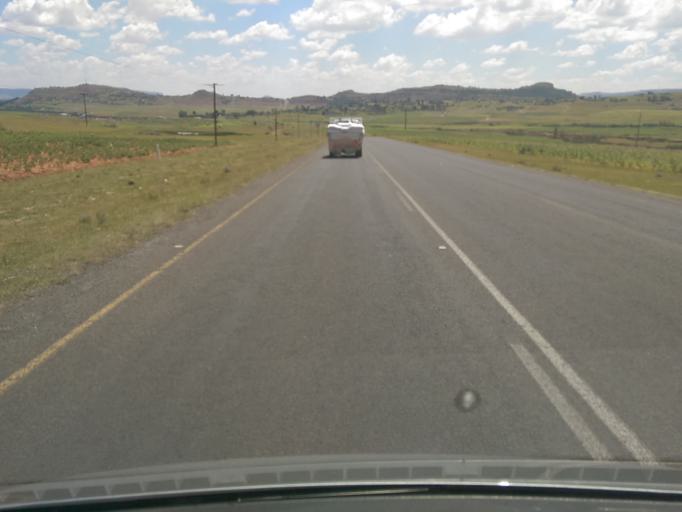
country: LS
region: Maseru
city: Maseru
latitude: -29.4218
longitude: 27.6656
